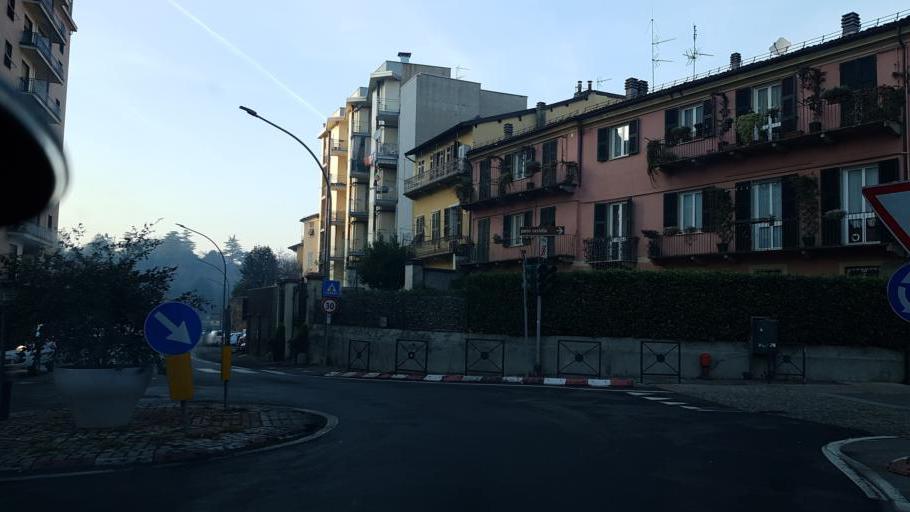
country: IT
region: Piedmont
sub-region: Provincia di Alessandria
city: Novi Ligure
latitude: 44.7580
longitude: 8.7843
